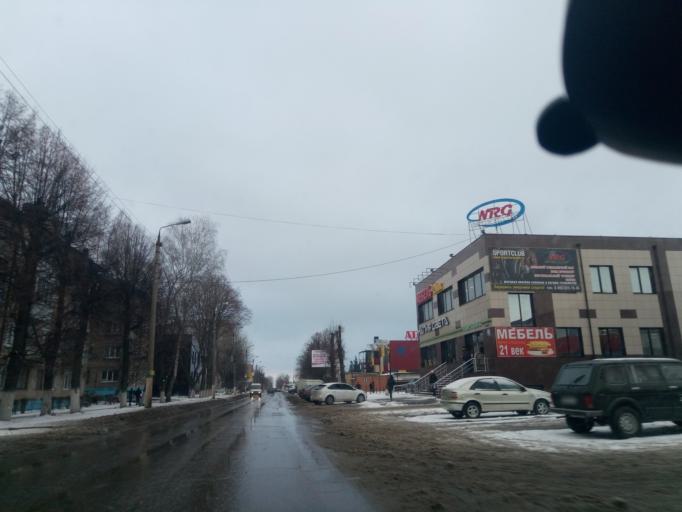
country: RU
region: Tula
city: Novomoskovsk
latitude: 54.0046
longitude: 38.2917
